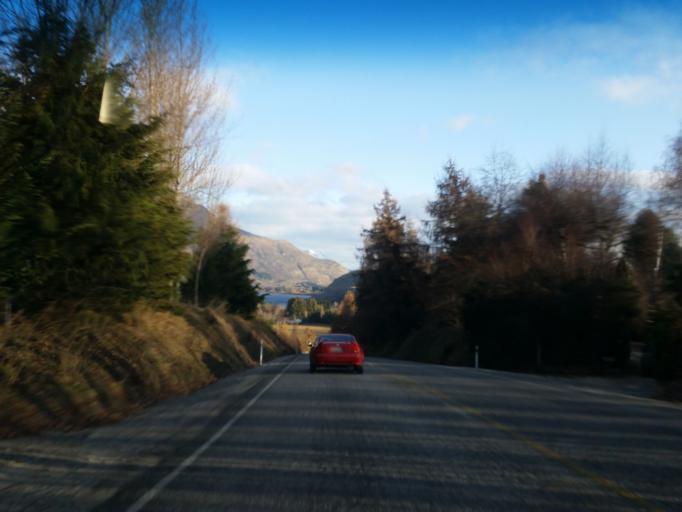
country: NZ
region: Otago
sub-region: Queenstown-Lakes District
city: Arrowtown
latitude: -44.9528
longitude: 168.8196
